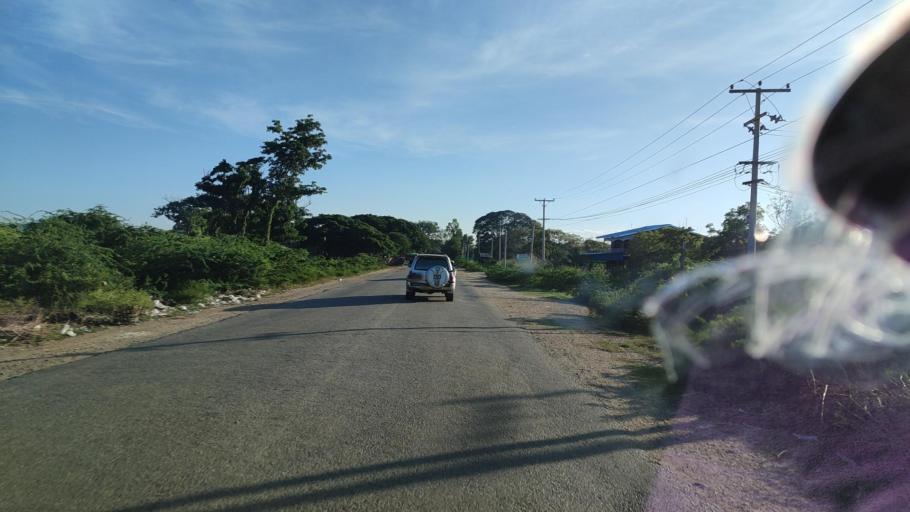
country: MM
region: Mandalay
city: Yamethin
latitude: 20.5956
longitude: 96.0686
